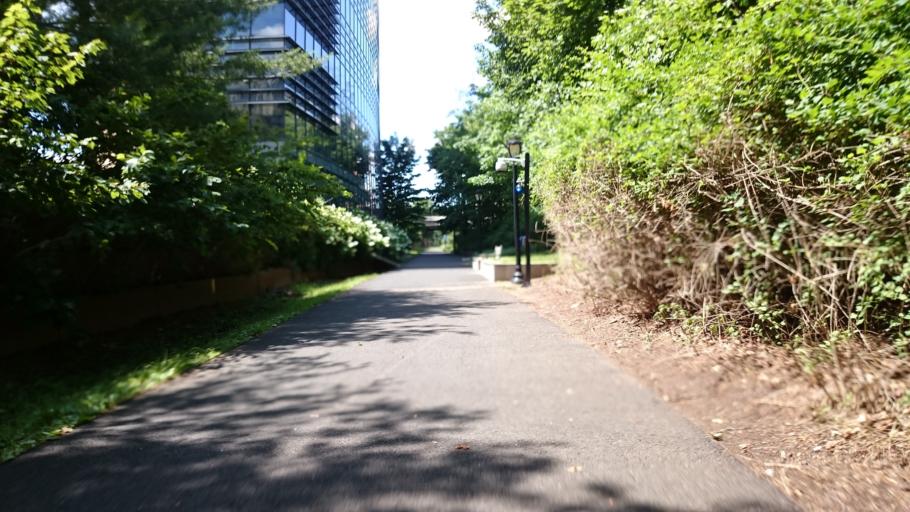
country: US
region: Connecticut
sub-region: New Haven County
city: New Haven
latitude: 41.3128
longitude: -72.9240
